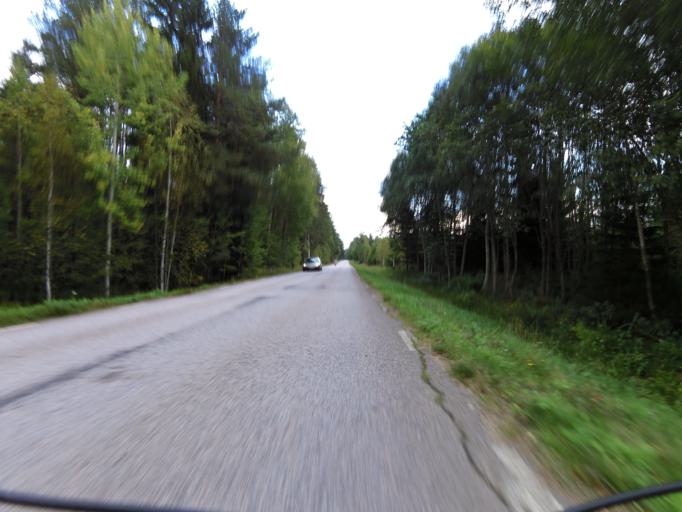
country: SE
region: Gaevleborg
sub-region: Sandvikens Kommun
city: Sandviken
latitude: 60.6660
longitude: 16.8779
